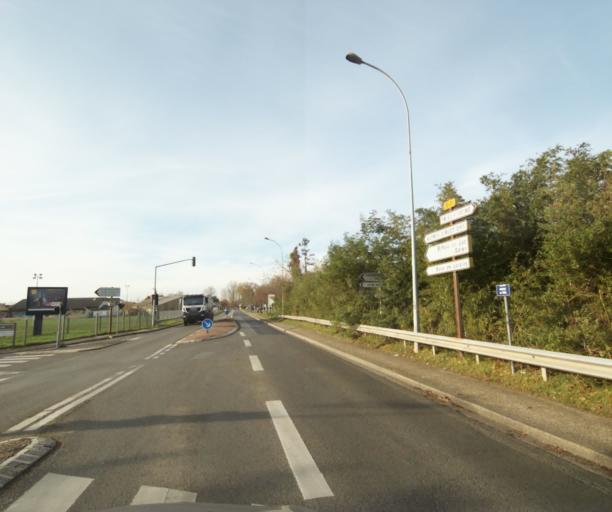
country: FR
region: Ile-de-France
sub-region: Departement des Yvelines
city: Triel-sur-Seine
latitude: 48.9780
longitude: 1.9960
